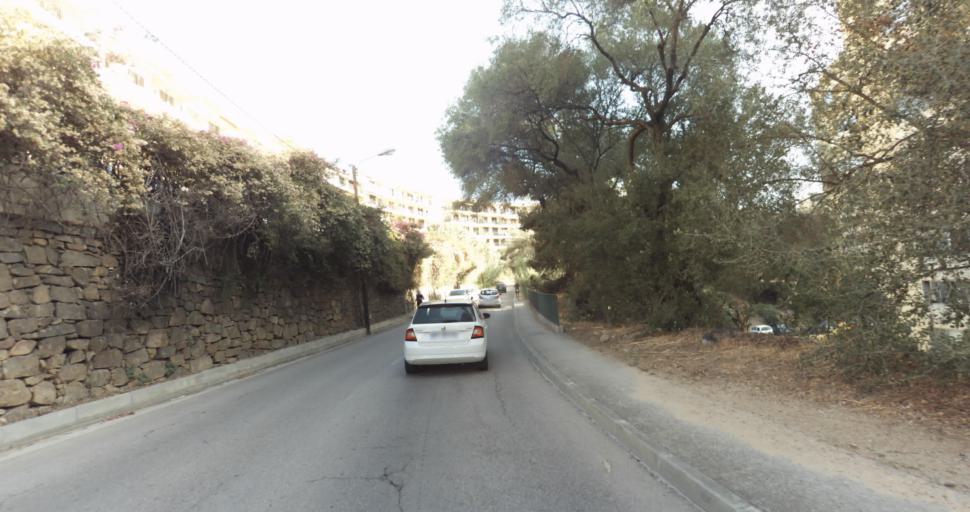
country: FR
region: Corsica
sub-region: Departement de la Corse-du-Sud
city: Ajaccio
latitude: 41.9197
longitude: 8.7264
